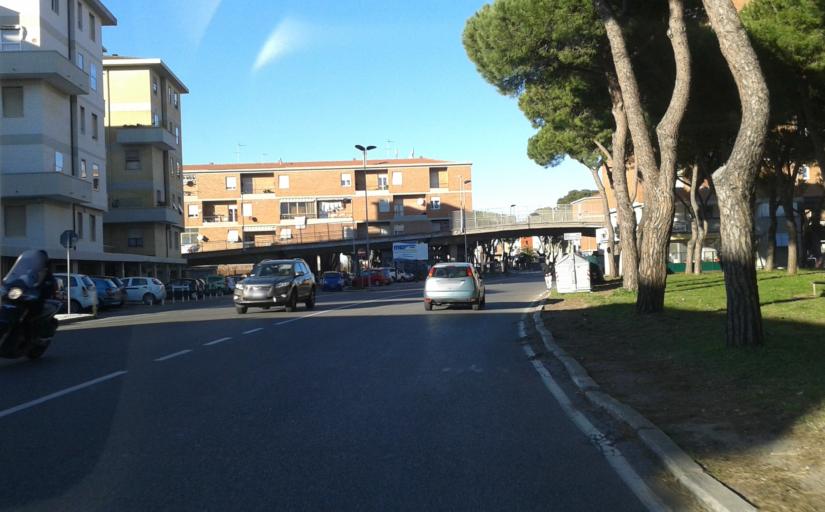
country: IT
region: Tuscany
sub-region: Provincia di Livorno
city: Livorno
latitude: 43.5234
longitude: 10.3231
